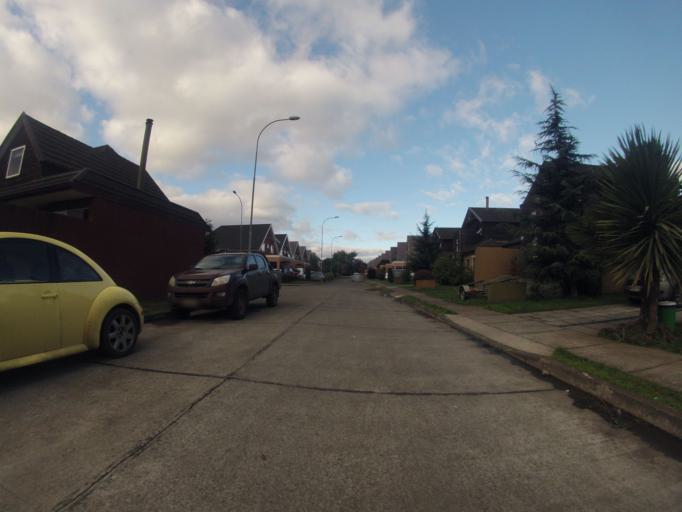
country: CL
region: Araucania
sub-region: Provincia de Cautin
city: Temuco
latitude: -38.7356
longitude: -72.6475
